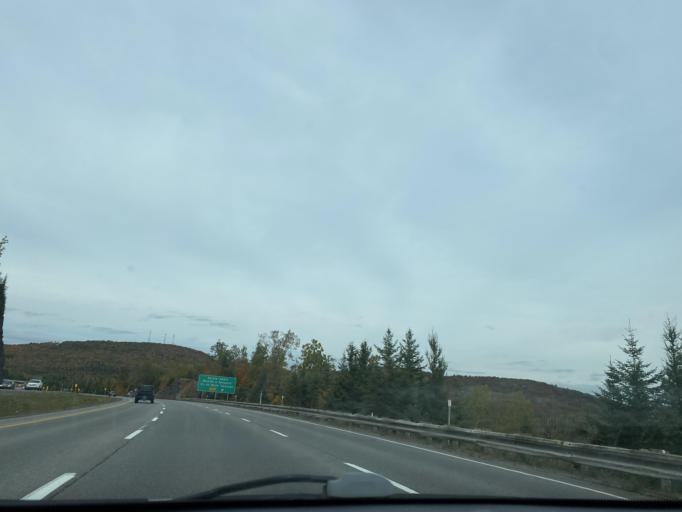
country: CA
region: Quebec
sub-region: Laurentides
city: Sainte-Adele
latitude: 45.9699
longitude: -74.1524
